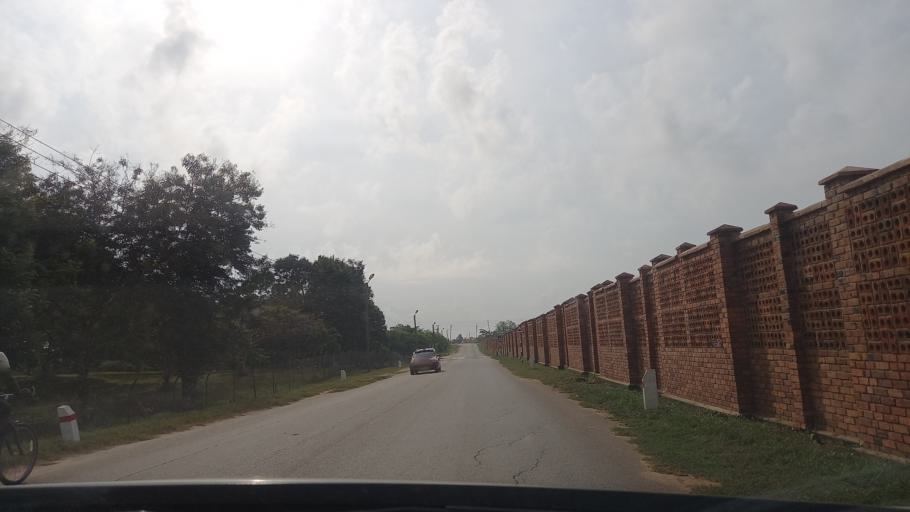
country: GH
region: Western
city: Shama Junction
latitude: 4.9758
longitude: -1.6578
